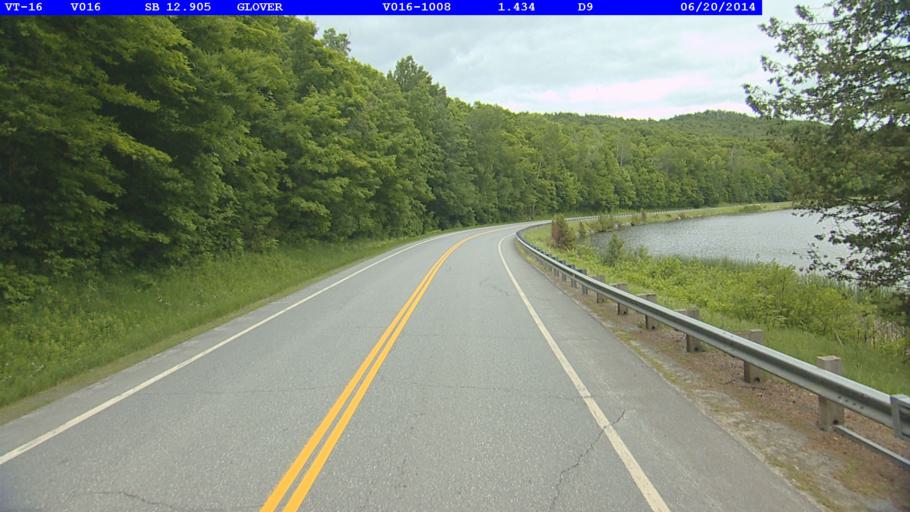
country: US
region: Vermont
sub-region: Caledonia County
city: Hardwick
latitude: 44.6456
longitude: -72.2017
